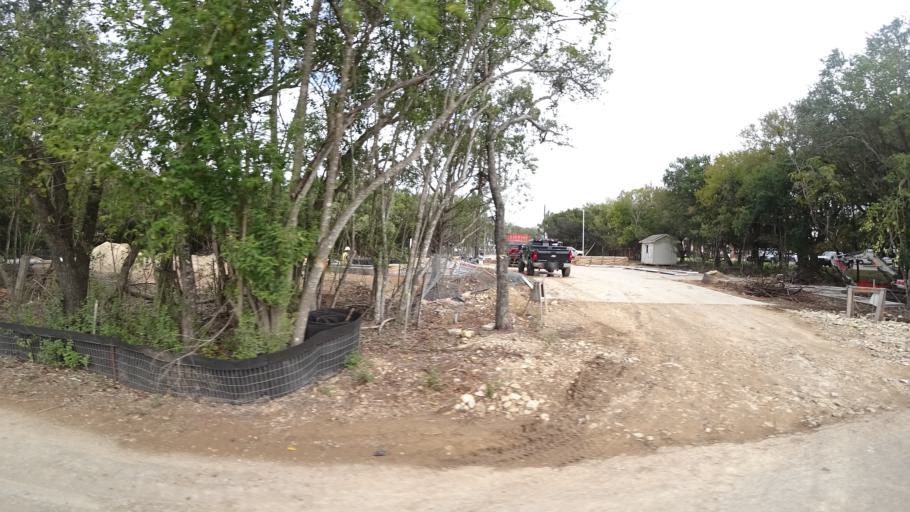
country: US
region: Texas
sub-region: Travis County
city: Shady Hollow
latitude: 30.2077
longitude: -97.8300
